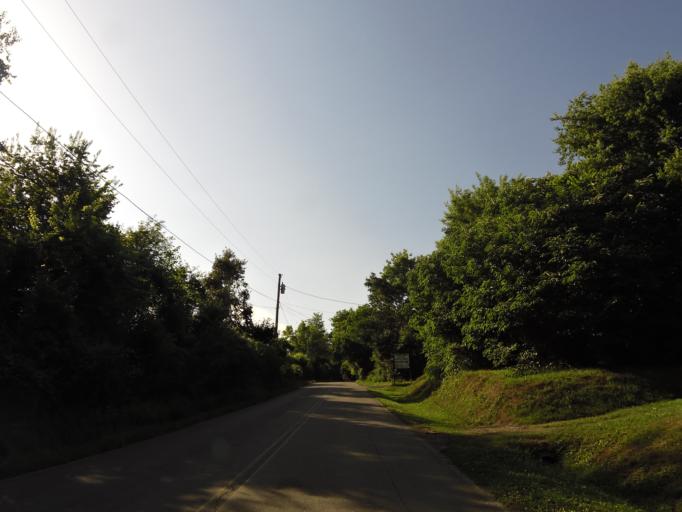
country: US
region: Tennessee
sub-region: Blount County
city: Alcoa
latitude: 35.8150
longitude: -83.9628
